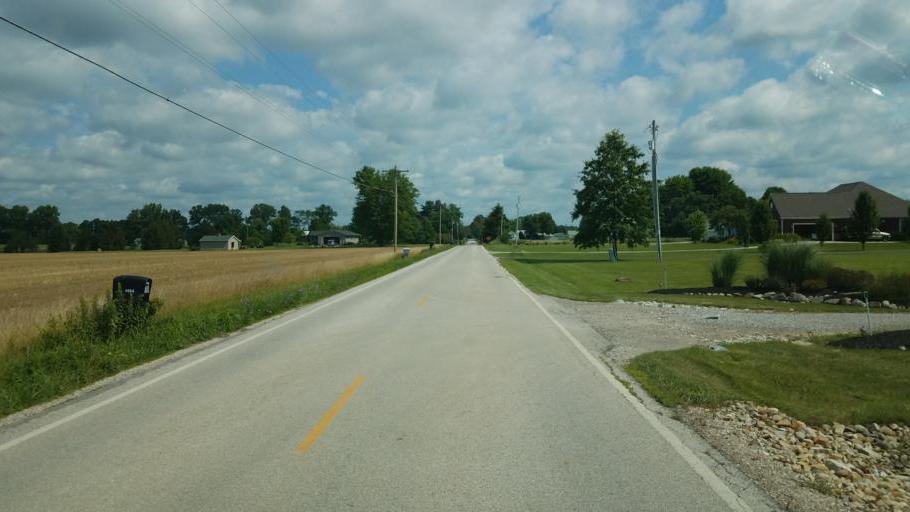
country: US
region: Ohio
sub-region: Delaware County
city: Ashley
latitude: 40.3247
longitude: -82.9322
